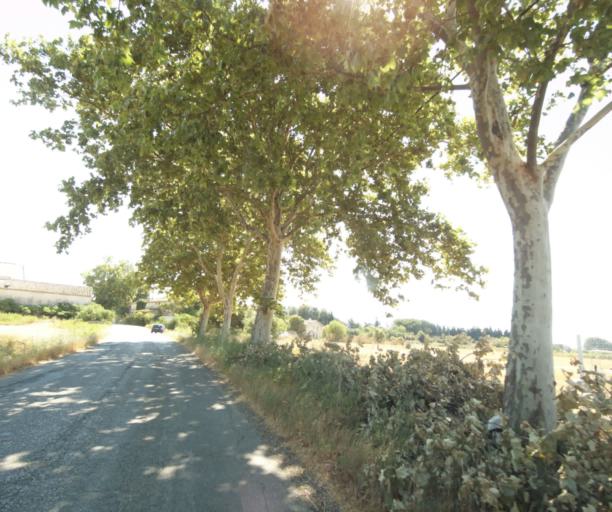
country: FR
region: Languedoc-Roussillon
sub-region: Departement de l'Herault
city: Marsillargues
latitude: 43.6624
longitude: 4.1612
